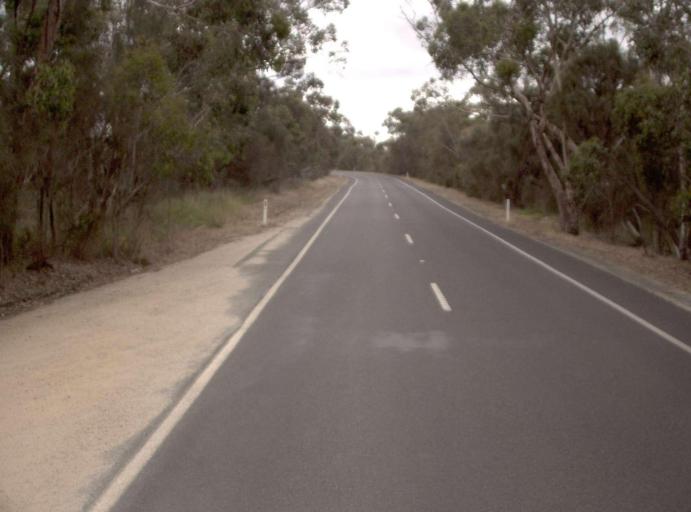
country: AU
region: Victoria
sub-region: Wellington
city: Sale
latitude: -38.2045
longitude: 147.0725
